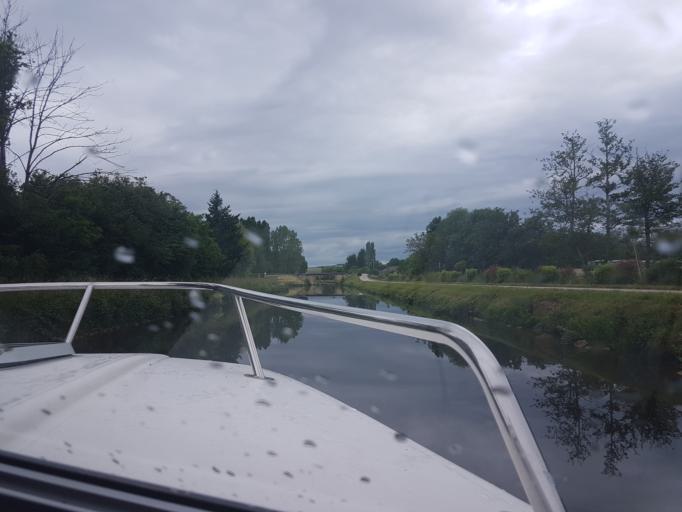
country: FR
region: Bourgogne
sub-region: Departement de l'Yonne
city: Saint-Bris-le-Vineux
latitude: 47.7080
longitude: 3.6364
